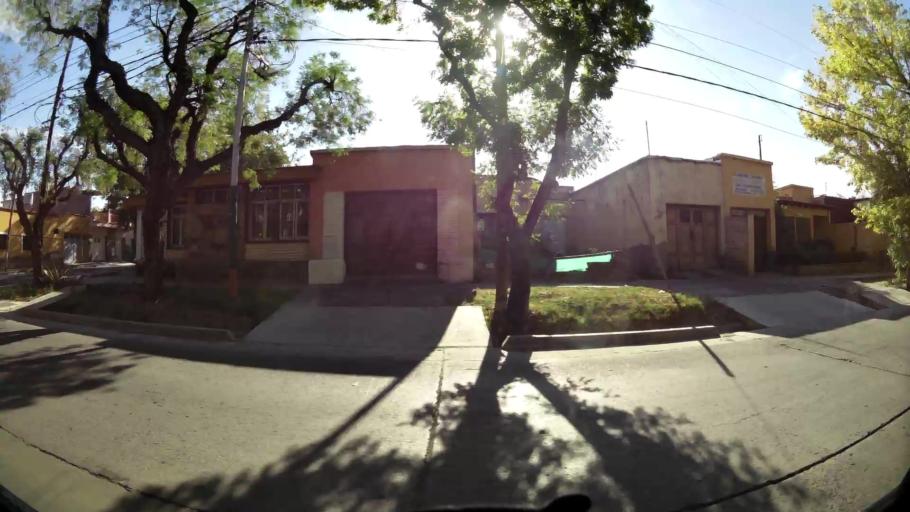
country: AR
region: Mendoza
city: Mendoza
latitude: -32.9025
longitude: -68.8246
